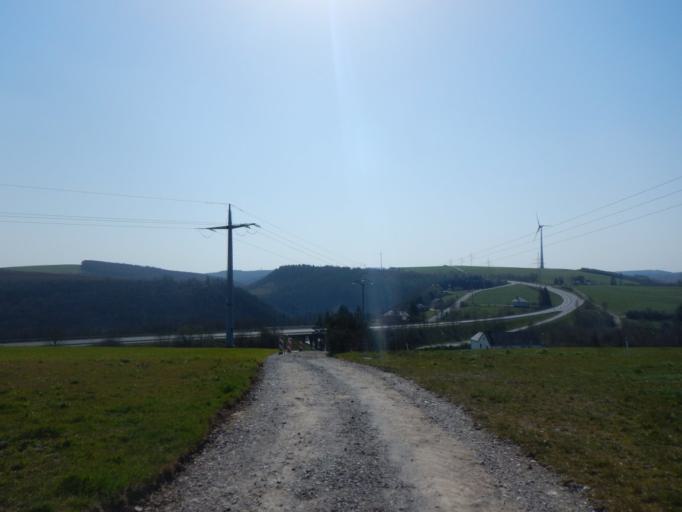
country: LU
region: Diekirch
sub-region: Canton de Diekirch
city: Bourscheid
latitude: 49.9400
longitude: 6.0840
